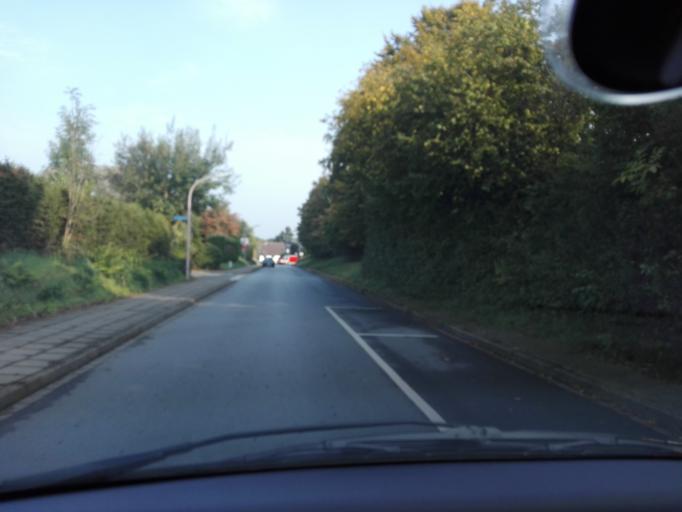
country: DE
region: North Rhine-Westphalia
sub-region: Regierungsbezirk Arnsberg
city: Unna
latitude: 51.5406
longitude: 7.7245
